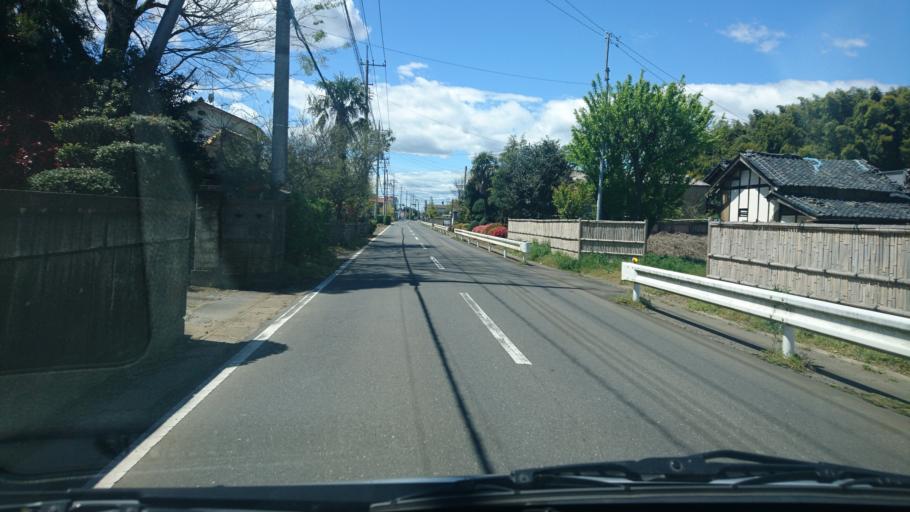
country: JP
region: Ibaraki
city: Shimodate
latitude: 36.2756
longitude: 139.9413
